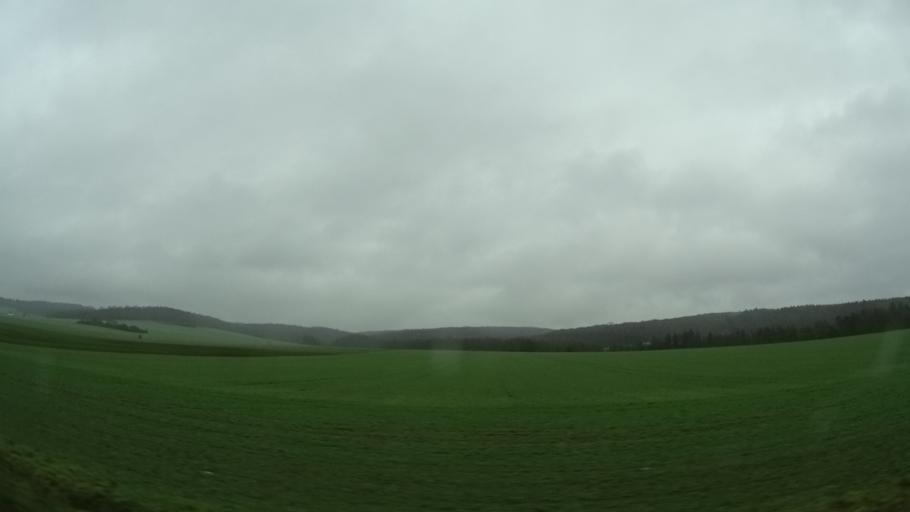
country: DE
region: Thuringia
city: Romhild
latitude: 50.4357
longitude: 10.5437
